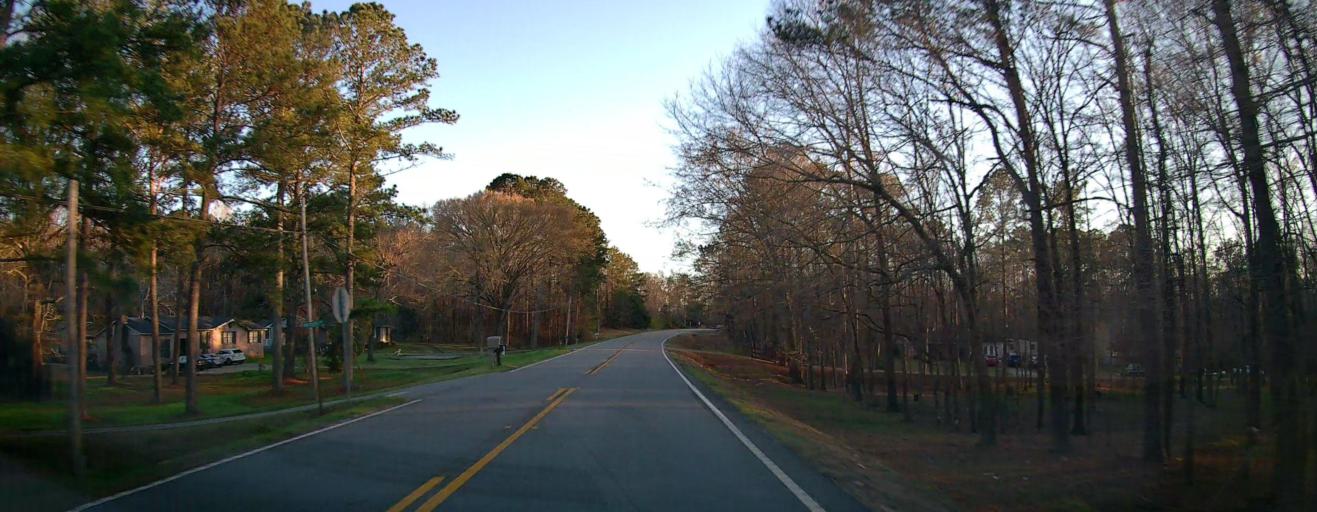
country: US
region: Alabama
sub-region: Lee County
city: Smiths Station
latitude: 32.6312
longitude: -85.0339
